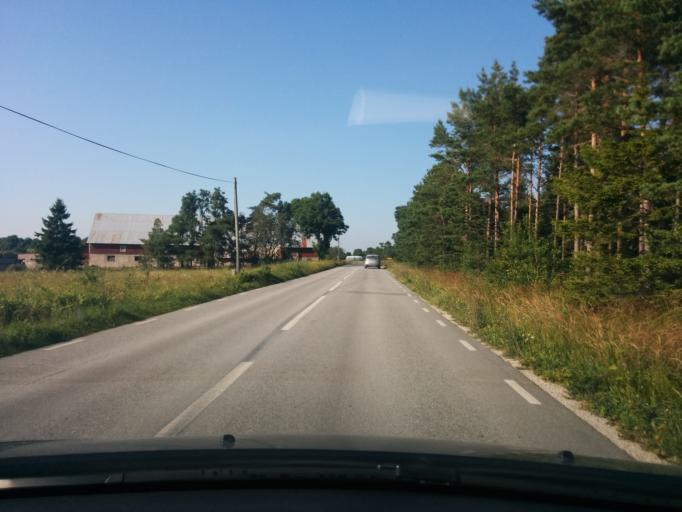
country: SE
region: Gotland
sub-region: Gotland
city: Slite
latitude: 57.6640
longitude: 18.7733
